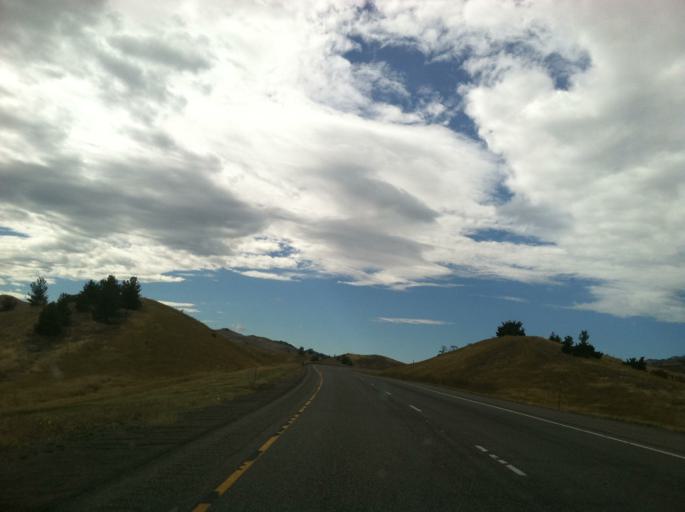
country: US
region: Montana
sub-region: Park County
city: Livingston
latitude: 45.6612
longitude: -110.6592
